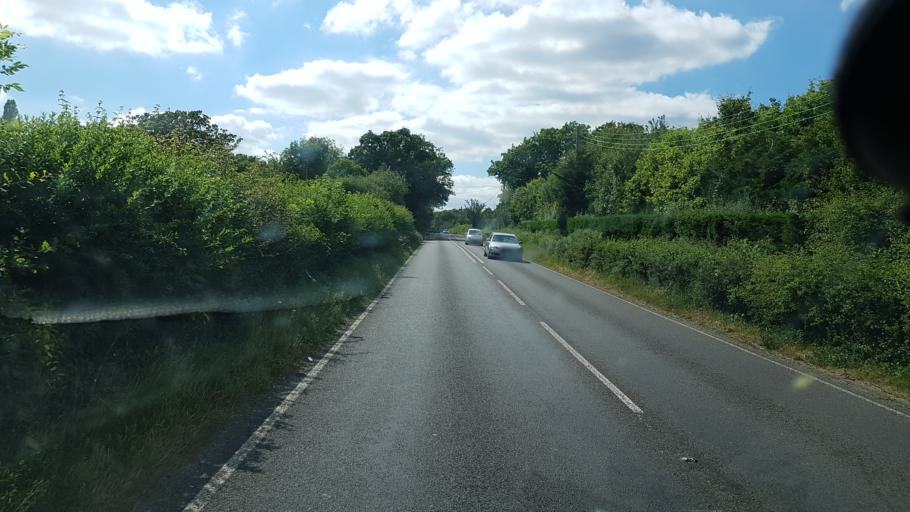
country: GB
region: England
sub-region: West Sussex
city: Partridge Green
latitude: 50.9922
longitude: -0.2893
